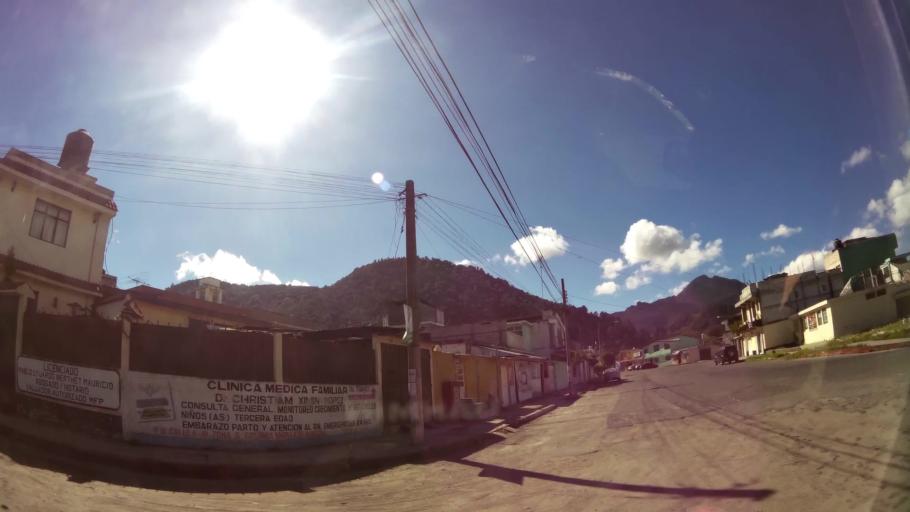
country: GT
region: Quetzaltenango
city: Quetzaltenango
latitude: 14.8380
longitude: -91.5057
